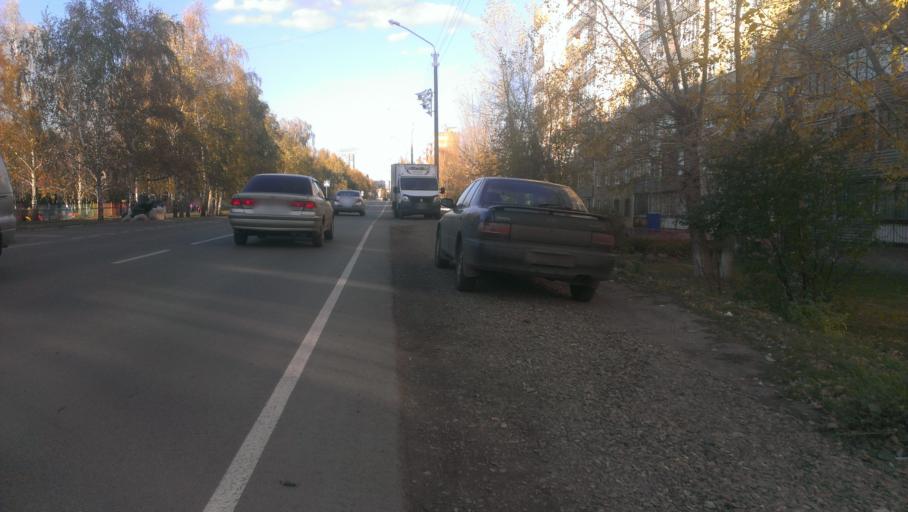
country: RU
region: Altai Krai
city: Novosilikatnyy
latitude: 53.3492
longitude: 83.6763
